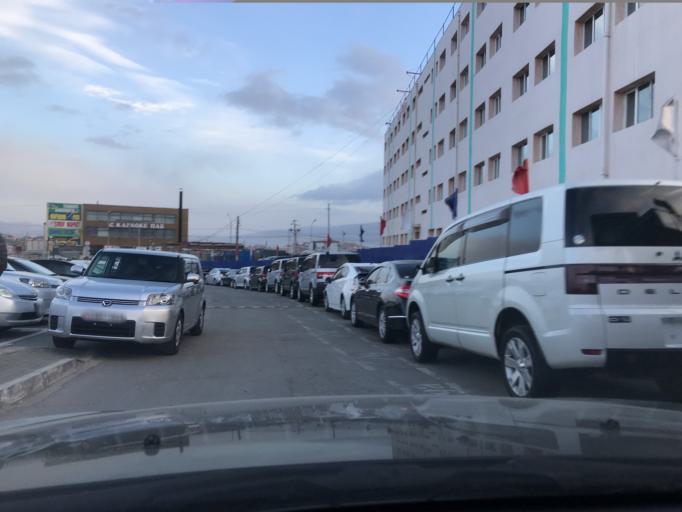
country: MN
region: Ulaanbaatar
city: Ulaanbaatar
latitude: 47.9292
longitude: 107.0026
